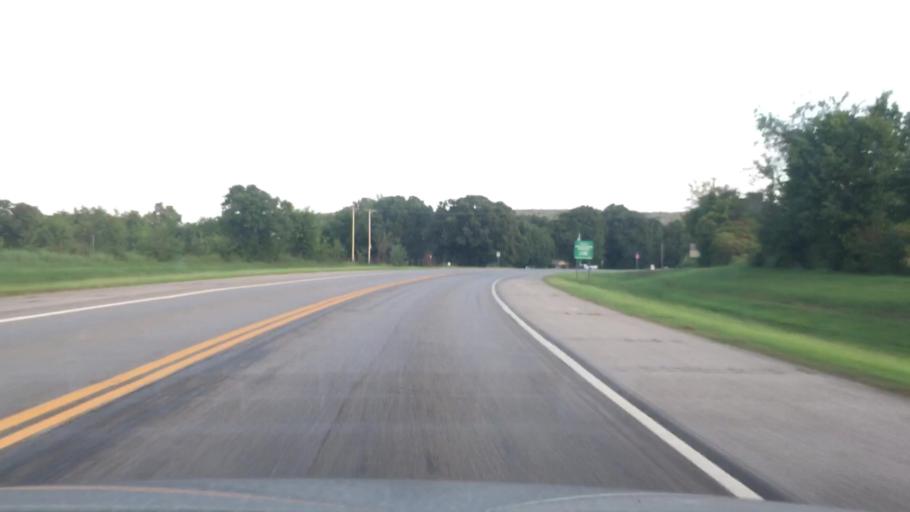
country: US
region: Oklahoma
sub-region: Cherokee County
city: Tahlequah
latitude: 35.9308
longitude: -95.1249
